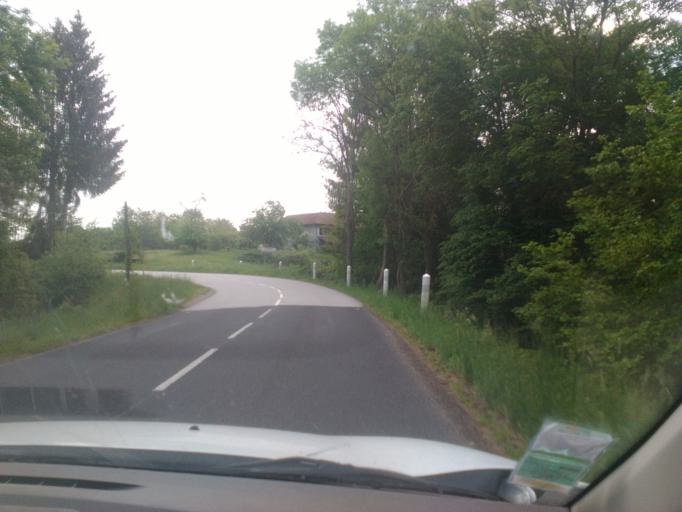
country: FR
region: Lorraine
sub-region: Departement des Vosges
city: Etival-Clairefontaine
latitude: 48.3598
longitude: 6.8285
